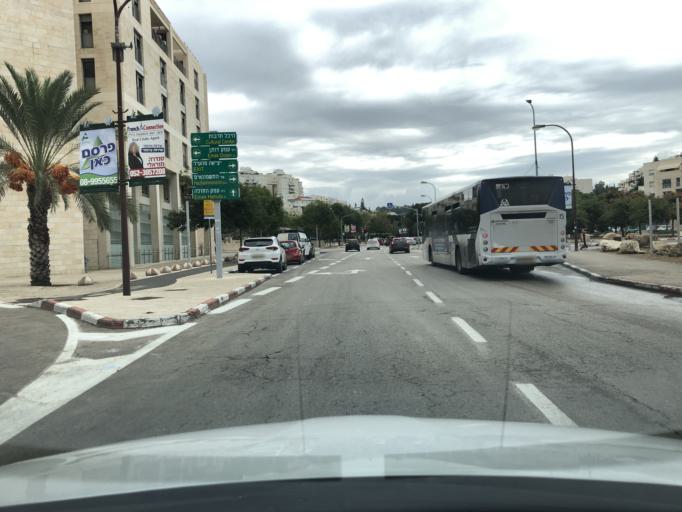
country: IL
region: Central District
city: Modiin
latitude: 31.8991
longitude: 35.0077
